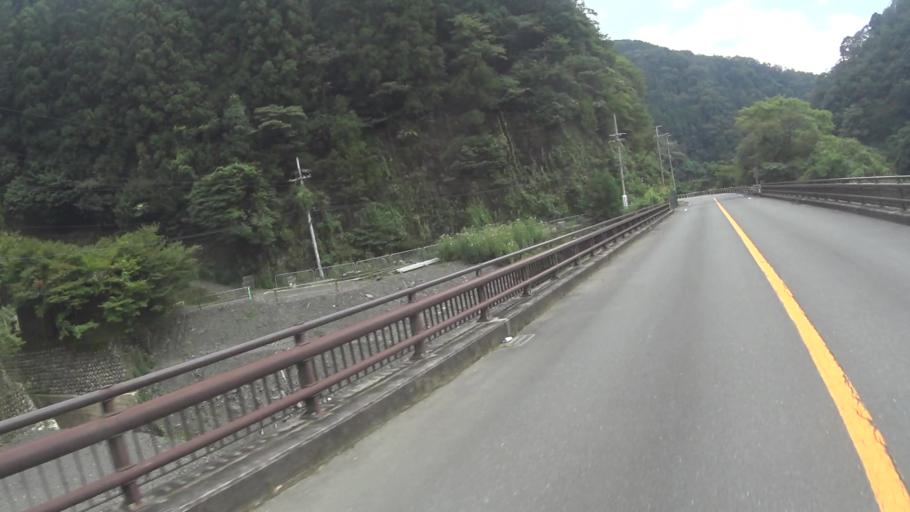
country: JP
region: Kyoto
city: Uji
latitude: 34.8745
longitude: 135.8449
